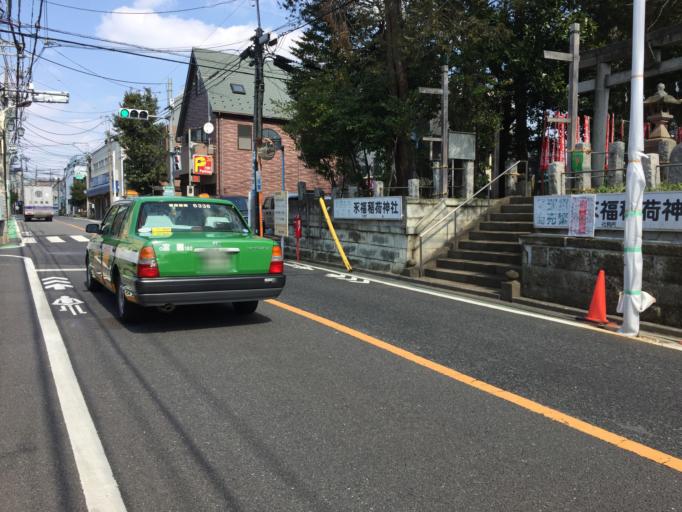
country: JP
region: Tokyo
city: Tokyo
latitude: 35.6724
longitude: 139.6426
